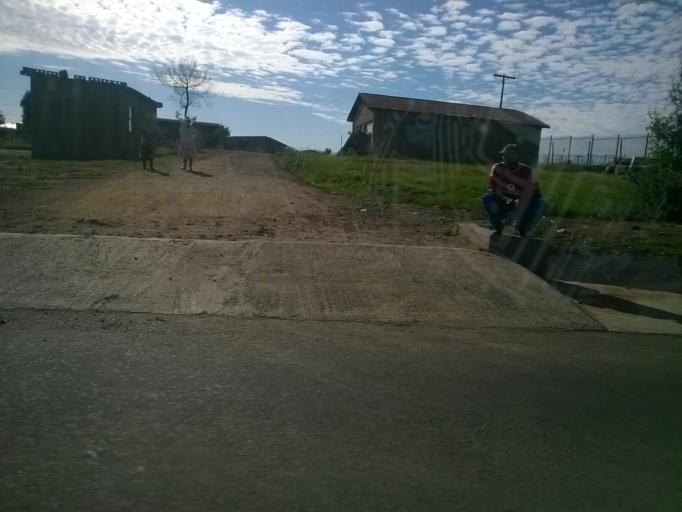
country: LS
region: Berea
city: Teyateyaneng
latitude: -29.1419
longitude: 27.7626
